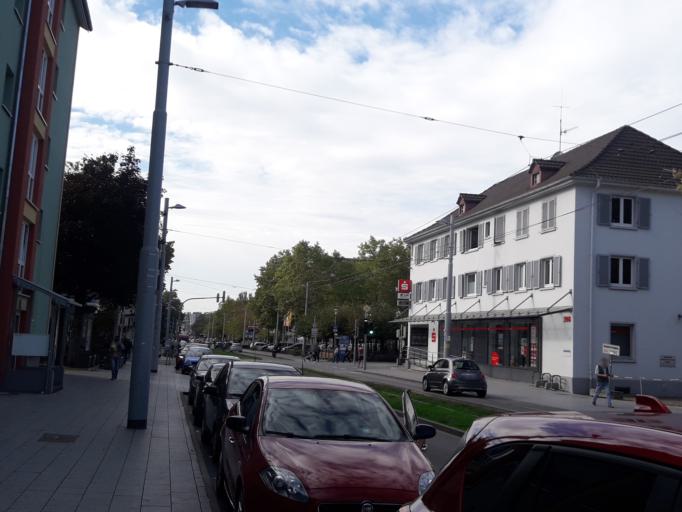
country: DE
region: Baden-Wuerttemberg
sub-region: Freiburg Region
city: Weil am Rhein
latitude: 47.5904
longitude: 7.5989
